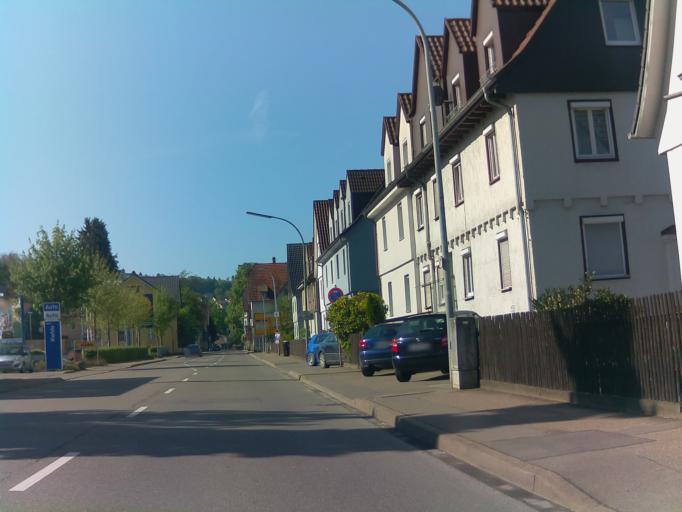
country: DE
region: Baden-Wuerttemberg
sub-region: Karlsruhe Region
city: Nagold
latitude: 48.5568
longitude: 8.7247
